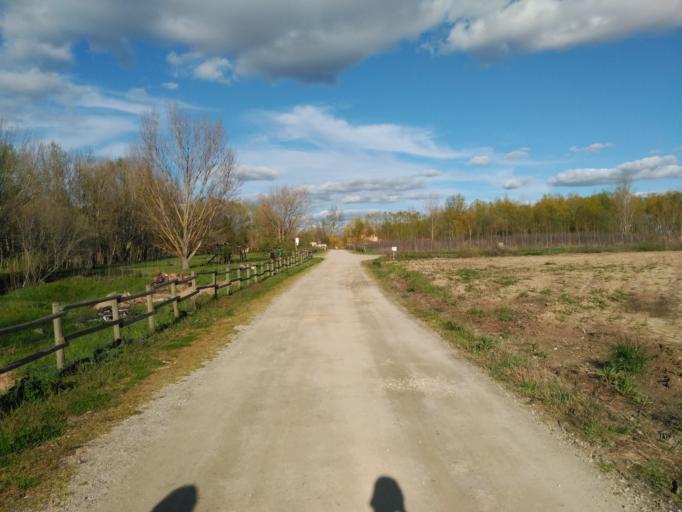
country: ES
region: Castille and Leon
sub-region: Provincia de Salamanca
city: Almenara de Tormes
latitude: 41.0559
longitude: -5.8229
